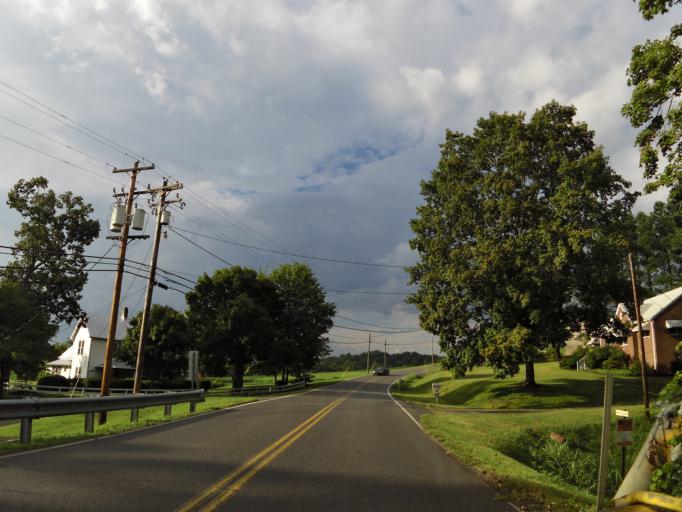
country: US
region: Tennessee
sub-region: Blount County
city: Wildwood
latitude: 35.8003
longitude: -83.8870
